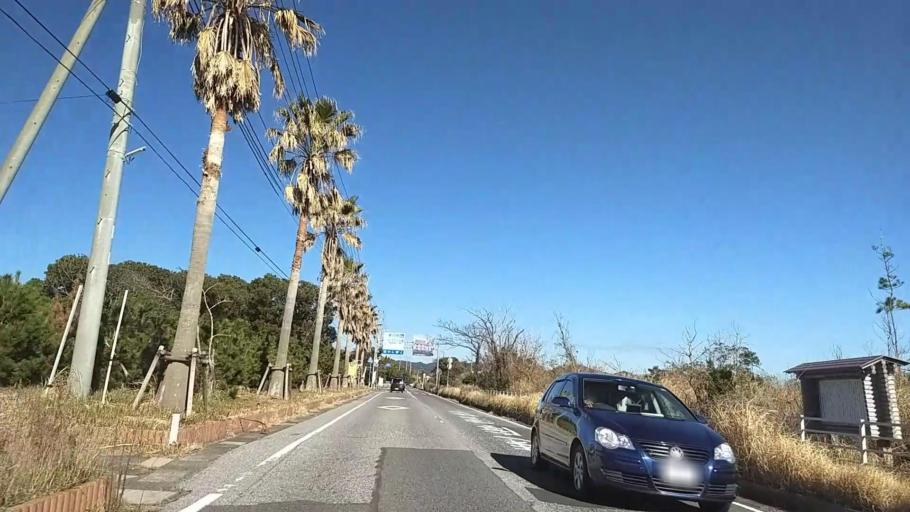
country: JP
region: Chiba
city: Tateyama
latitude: 35.0075
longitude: 139.9766
